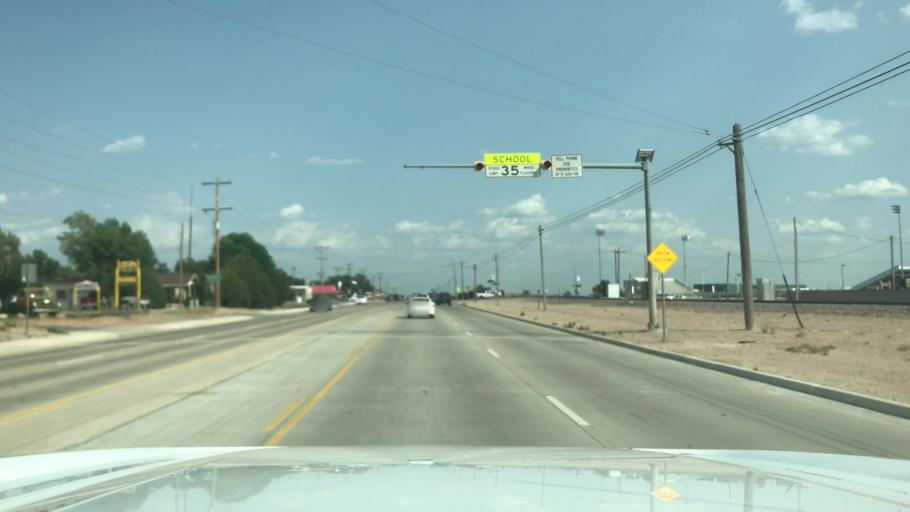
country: US
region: Texas
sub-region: Dallam County
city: Dalhart
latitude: 36.0521
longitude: -102.5025
